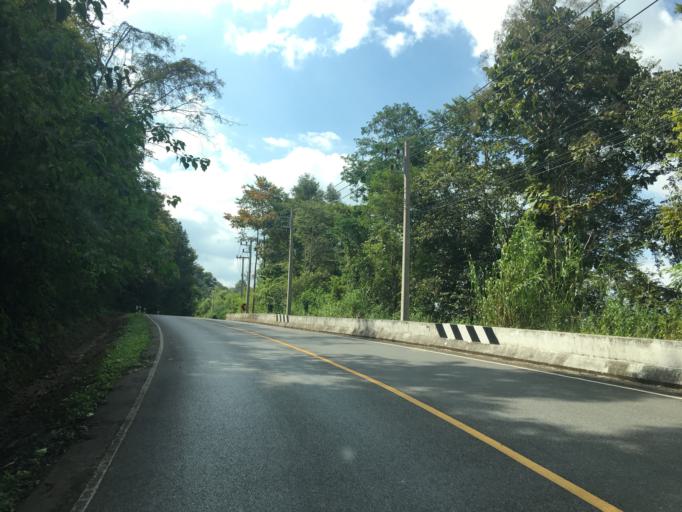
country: TH
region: Nan
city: Nan
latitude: 18.8667
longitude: 100.6239
